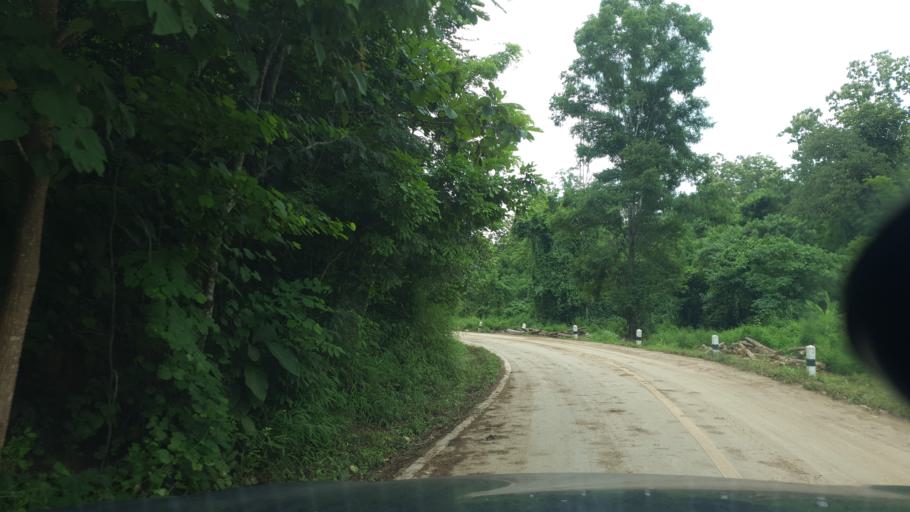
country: TH
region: Lampang
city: Hang Chat
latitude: 18.3717
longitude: 99.2605
